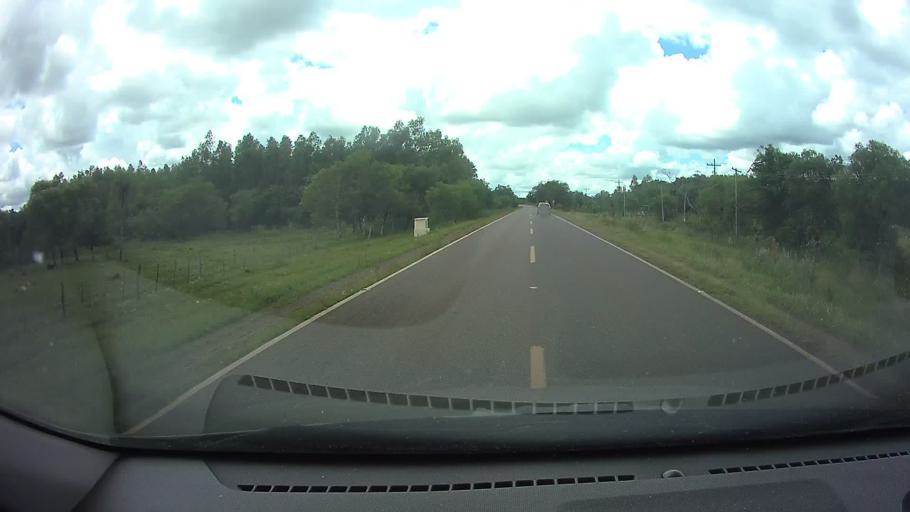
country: PY
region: Paraguari
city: Ybycui
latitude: -25.8978
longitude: -56.9660
